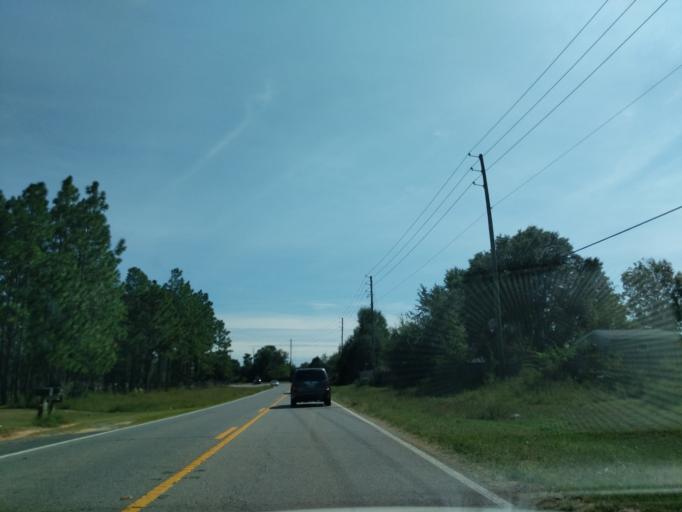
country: US
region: Florida
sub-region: Okaloosa County
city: Crestview
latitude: 30.7211
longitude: -86.6143
